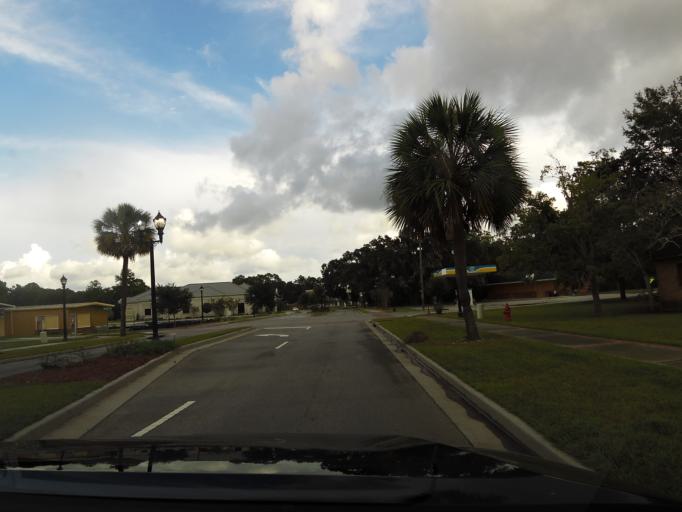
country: US
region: Georgia
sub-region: Liberty County
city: Hinesville
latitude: 31.8520
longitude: -81.6005
